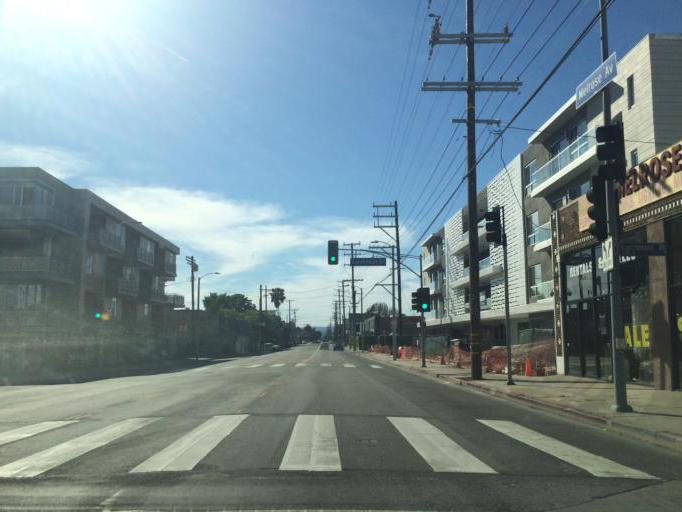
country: US
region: California
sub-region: Los Angeles County
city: Hollywood
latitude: 34.0835
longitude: -118.3234
